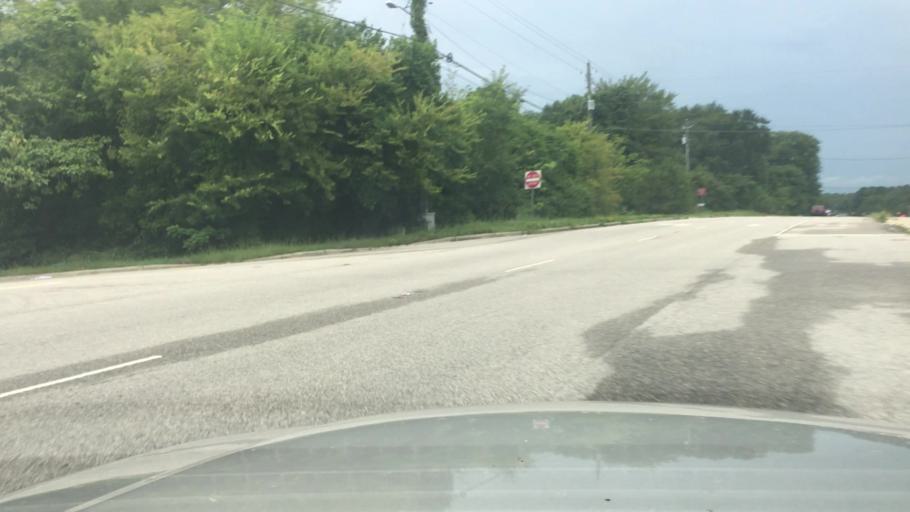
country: US
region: North Carolina
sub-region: Cumberland County
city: Hope Mills
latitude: 34.9986
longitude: -78.9724
